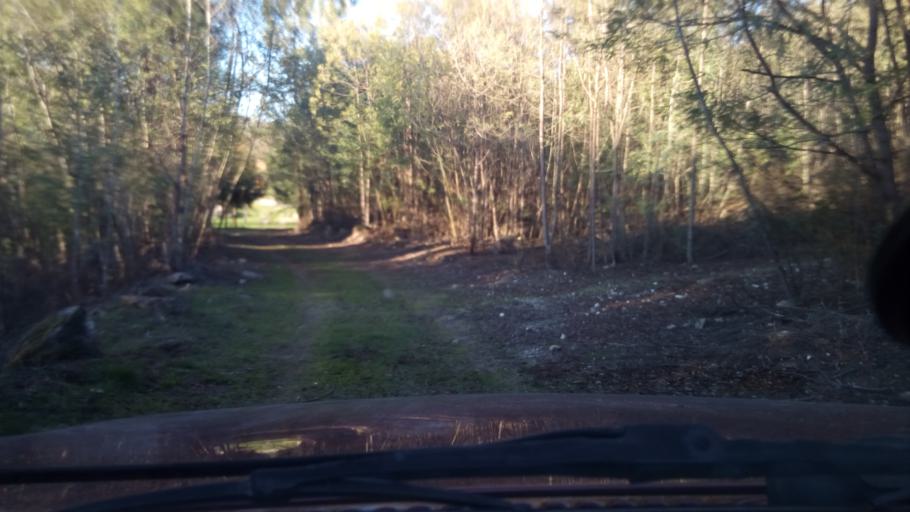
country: PT
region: Guarda
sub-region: Fornos de Algodres
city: Fornos de Algodres
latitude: 40.6095
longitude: -7.5348
